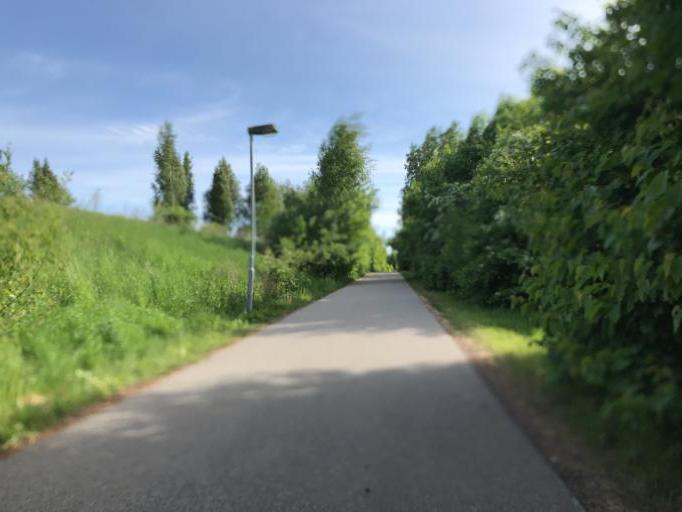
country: SE
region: Skane
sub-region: Malmo
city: Oxie
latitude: 55.5342
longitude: 13.0960
